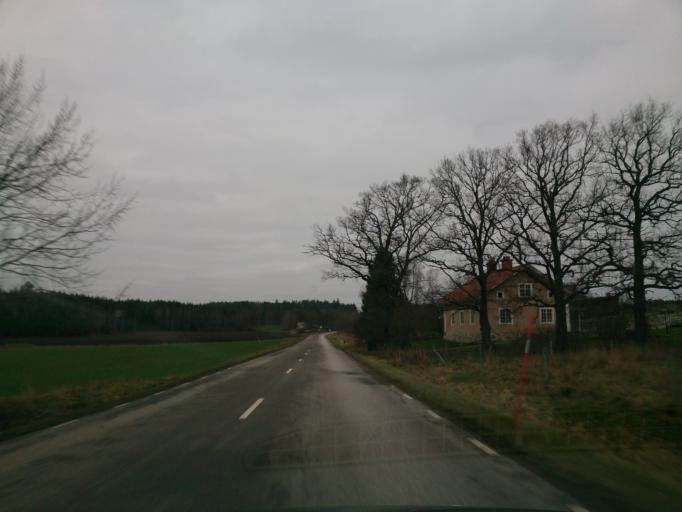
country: SE
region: OEstergoetland
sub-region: Atvidabergs Kommun
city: Atvidaberg
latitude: 58.3638
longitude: 16.0252
